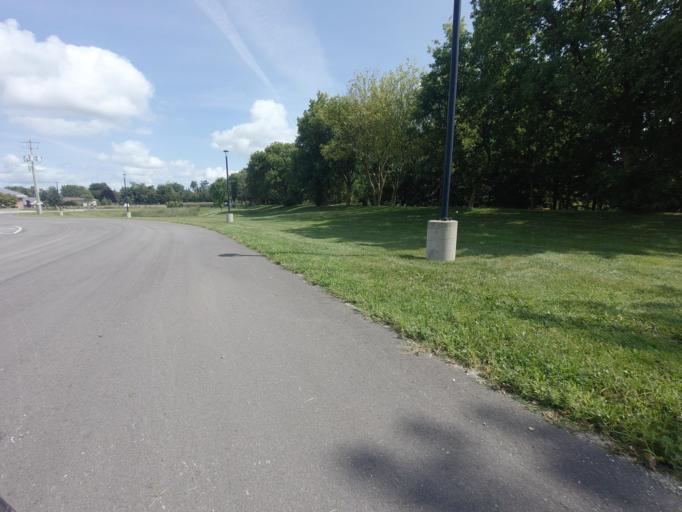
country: CA
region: Ontario
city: Waterloo
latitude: 43.5830
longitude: -80.7301
